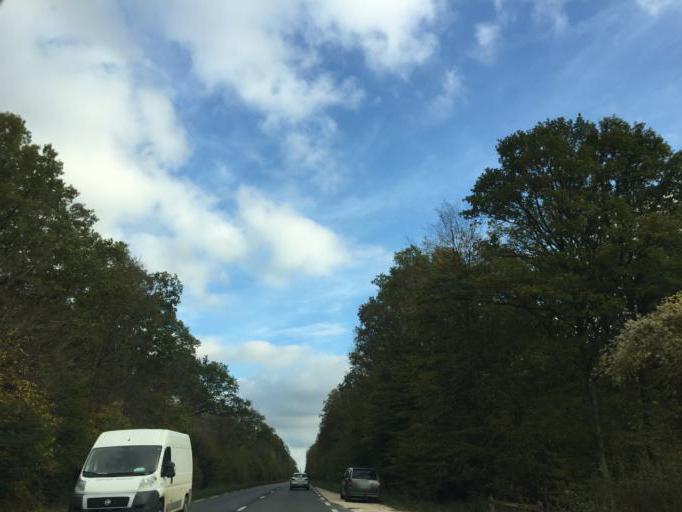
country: FR
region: Ile-de-France
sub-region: Departement de Seine-et-Marne
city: Villeneuve-le-Comte
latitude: 48.7974
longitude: 2.8581
